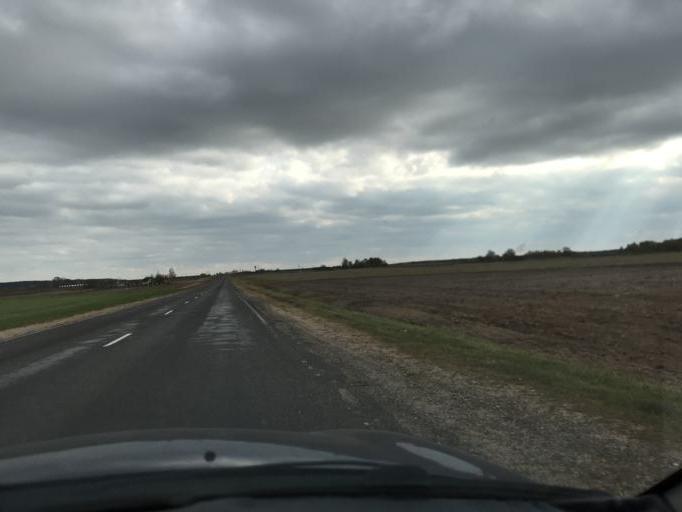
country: BY
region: Grodnenskaya
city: Lida
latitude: 53.8076
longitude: 25.1149
